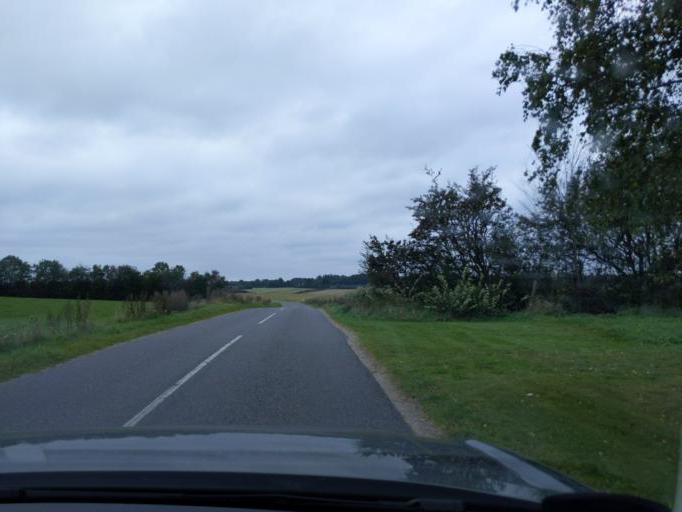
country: DK
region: North Denmark
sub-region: Mariagerfjord Kommune
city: Hobro
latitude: 56.5520
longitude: 9.6538
